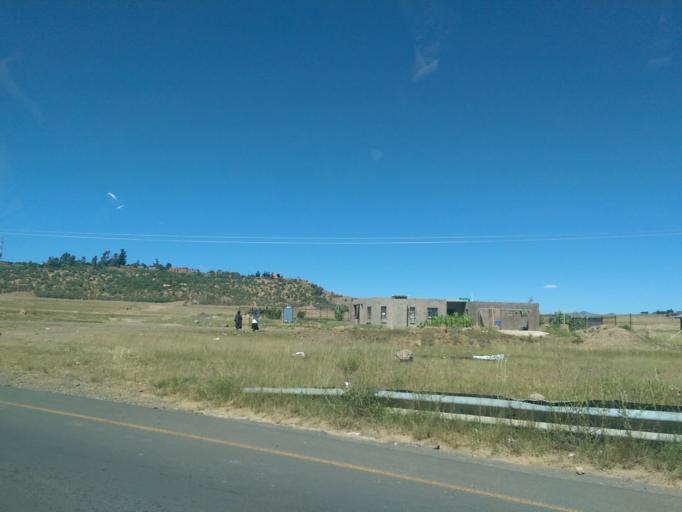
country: LS
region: Maseru
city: Maseru
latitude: -29.3868
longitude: 27.5605
